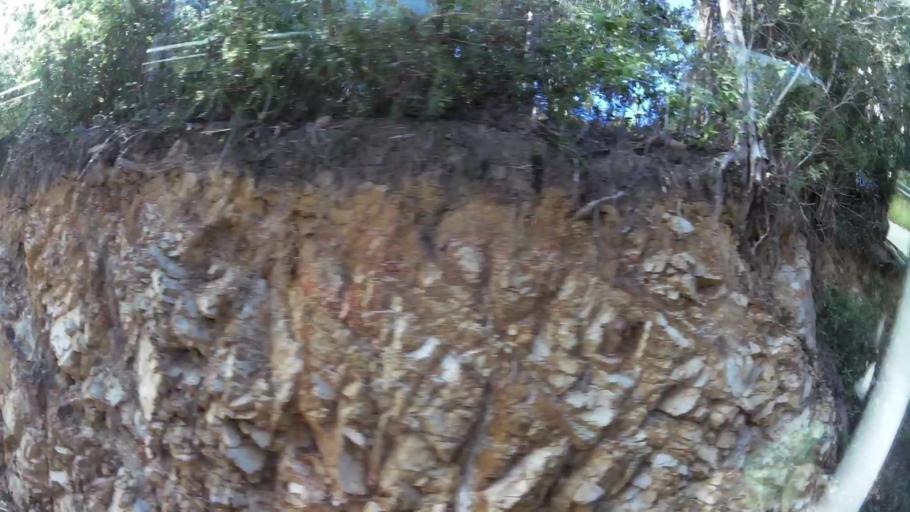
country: VG
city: Tortola
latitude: 18.4881
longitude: -64.3981
